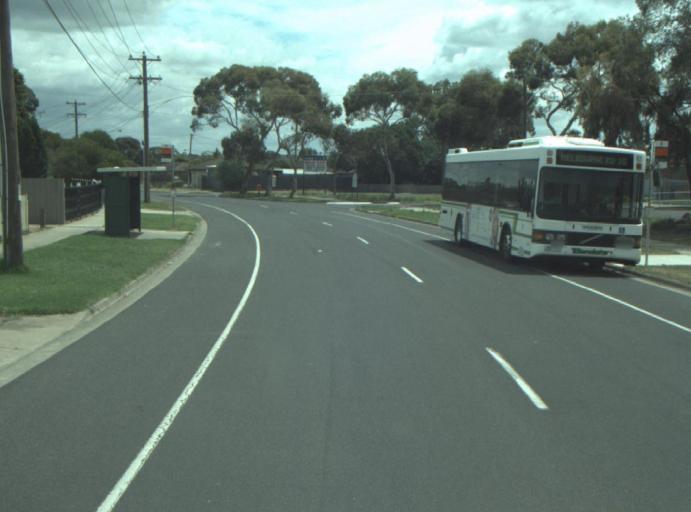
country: AU
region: Victoria
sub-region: Greater Geelong
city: Lara
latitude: -38.0651
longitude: 144.3737
